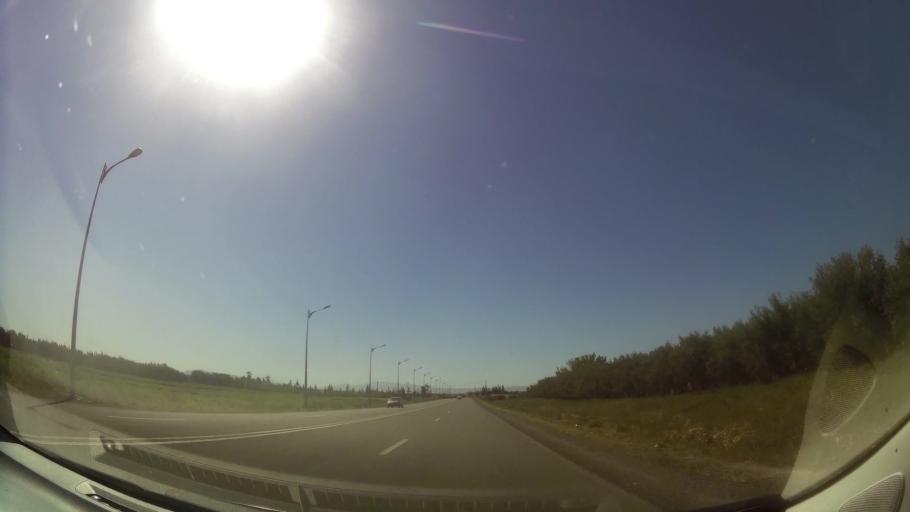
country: MA
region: Oriental
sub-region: Oujda-Angad
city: Oujda
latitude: 34.7368
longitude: -1.8814
